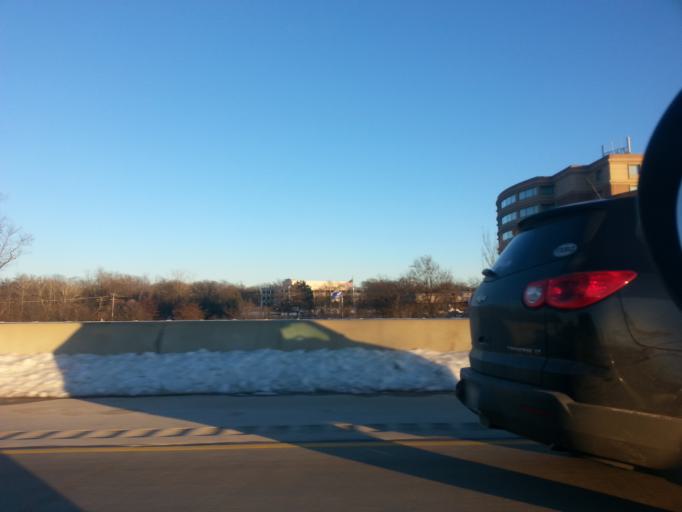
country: US
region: Illinois
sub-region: Cook County
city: Des Plaines
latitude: 42.0805
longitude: -87.8663
